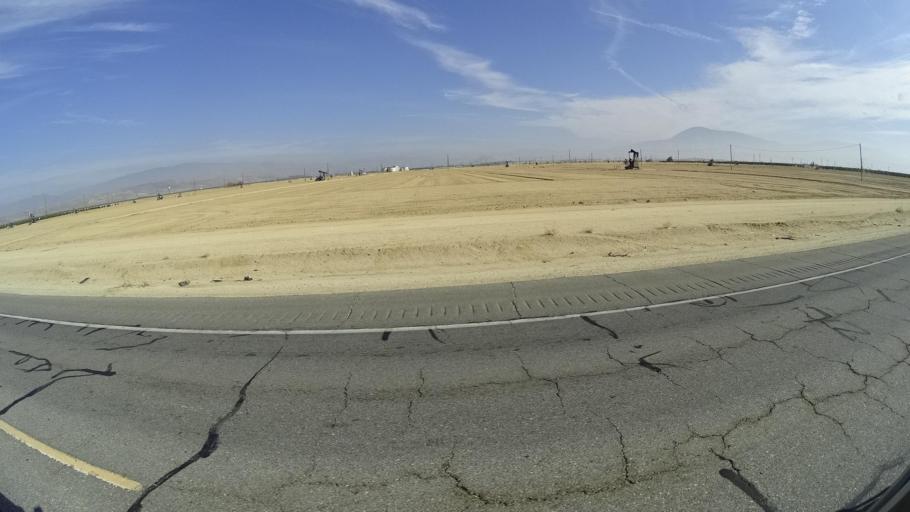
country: US
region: California
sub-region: Kern County
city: Lamont
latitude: 35.3226
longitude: -118.8431
